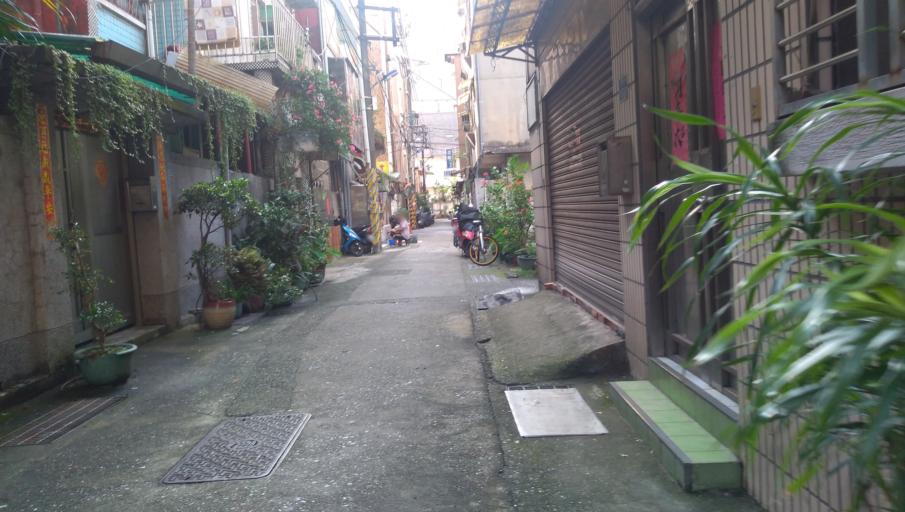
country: TW
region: Taiwan
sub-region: Keelung
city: Keelung
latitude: 25.1412
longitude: 121.7604
